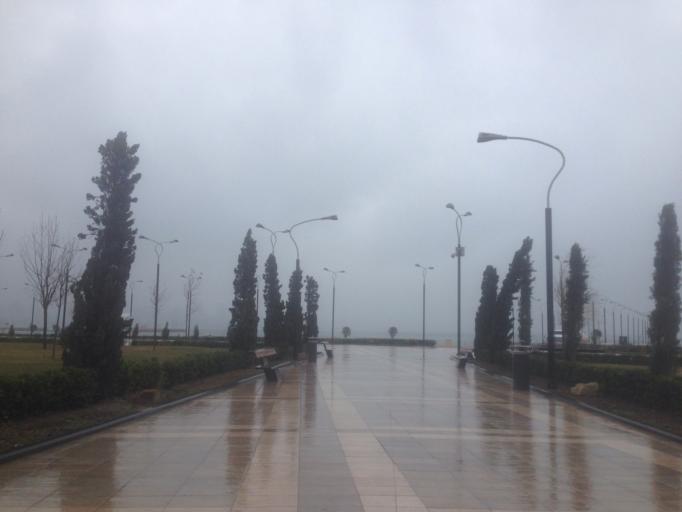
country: AZ
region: Baki
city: Badamdar
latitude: 40.3460
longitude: 49.8464
